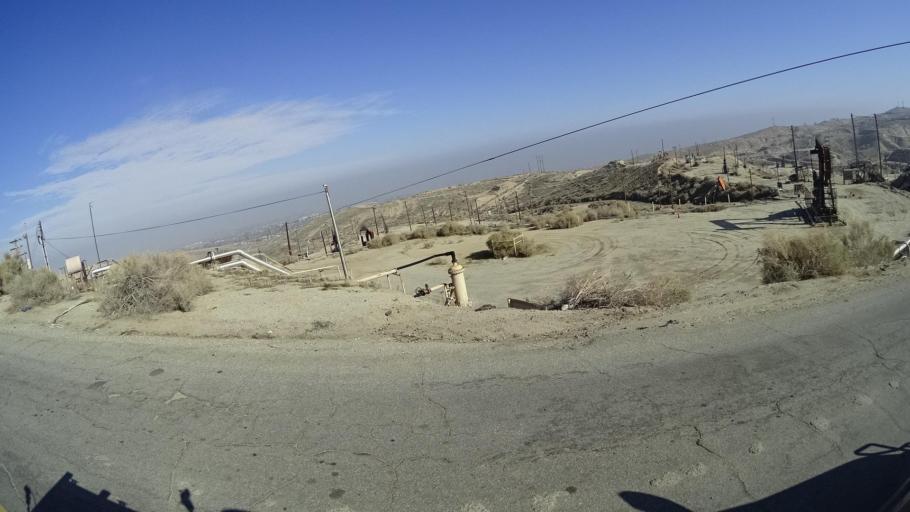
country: US
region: California
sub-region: Kern County
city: Taft Heights
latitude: 35.1207
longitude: -119.4749
